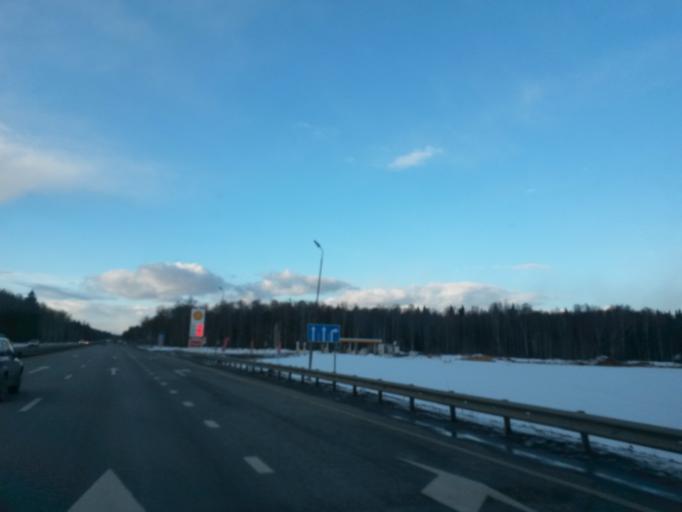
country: RU
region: Moskovskaya
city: Ashukino
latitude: 56.1546
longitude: 38.0122
